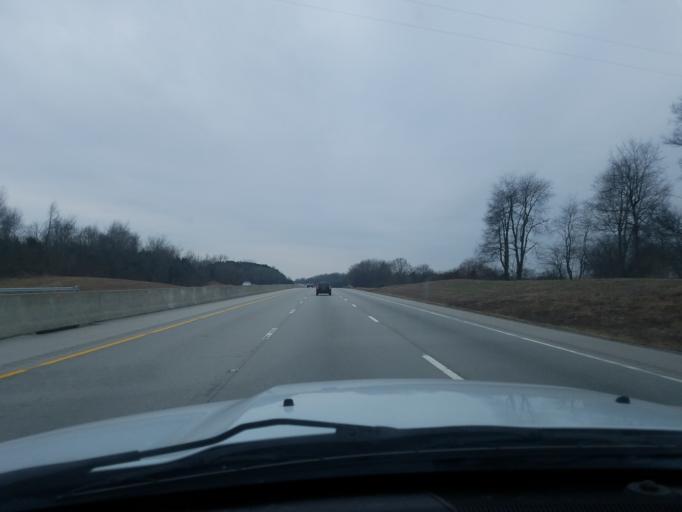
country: US
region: Kentucky
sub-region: Barren County
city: Cave City
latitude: 37.0808
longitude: -86.0716
